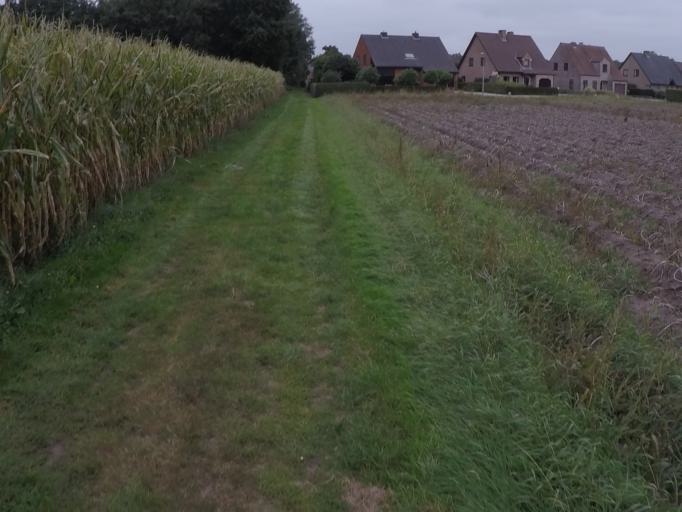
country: BE
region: Flanders
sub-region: Provincie Antwerpen
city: Kasterlee
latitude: 51.2276
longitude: 4.9710
